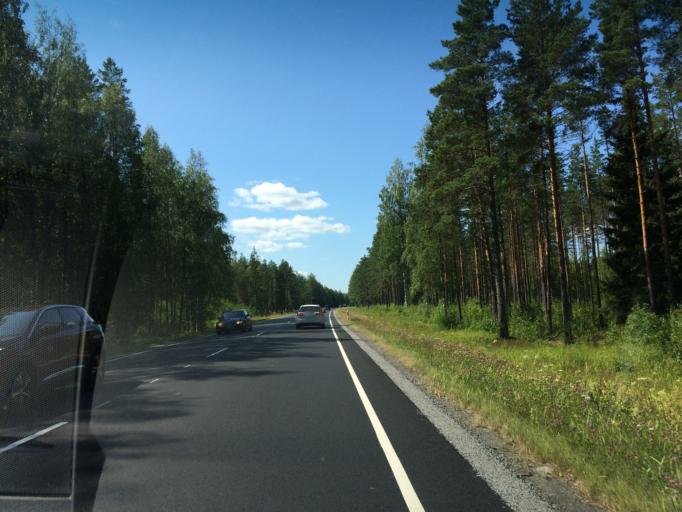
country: FI
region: Pirkanmaa
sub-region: Lounais-Pirkanmaa
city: Kiikoinen
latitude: 61.4734
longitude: 22.5277
